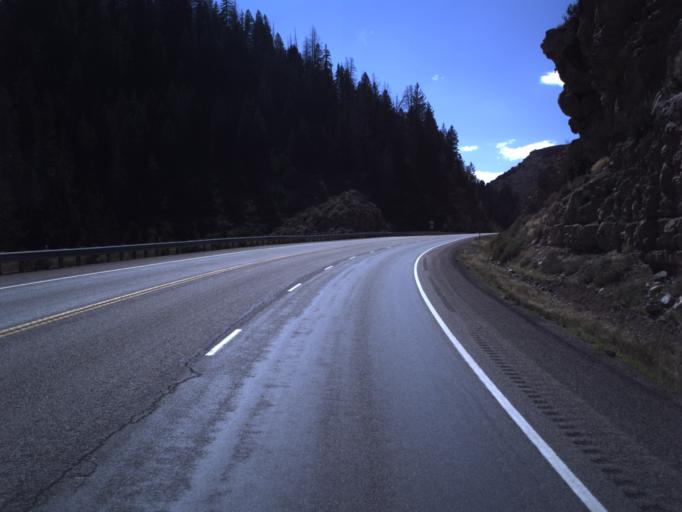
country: US
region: Utah
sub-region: Carbon County
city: Helper
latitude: 40.1941
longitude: -110.9352
